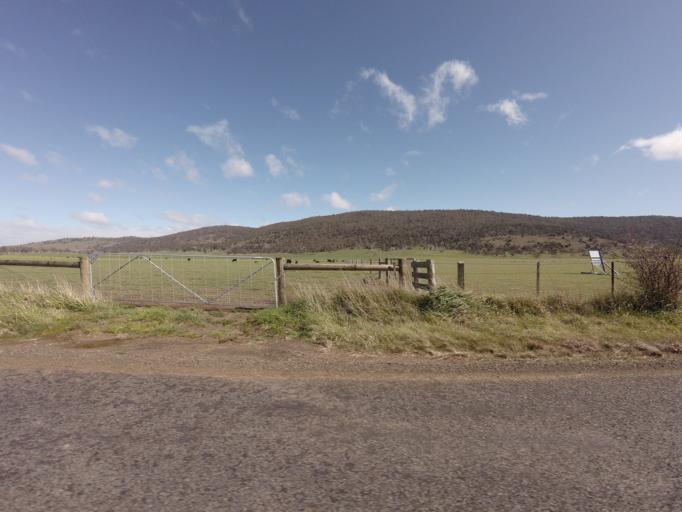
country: AU
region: Tasmania
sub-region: Northern Midlands
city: Evandale
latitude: -41.9740
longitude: 147.4448
